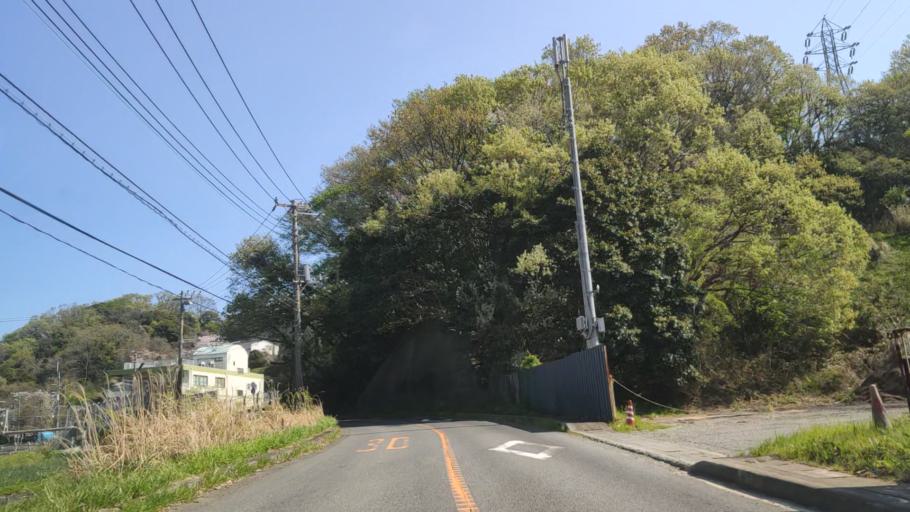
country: JP
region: Kanagawa
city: Ninomiya
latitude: 35.3142
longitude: 139.2729
